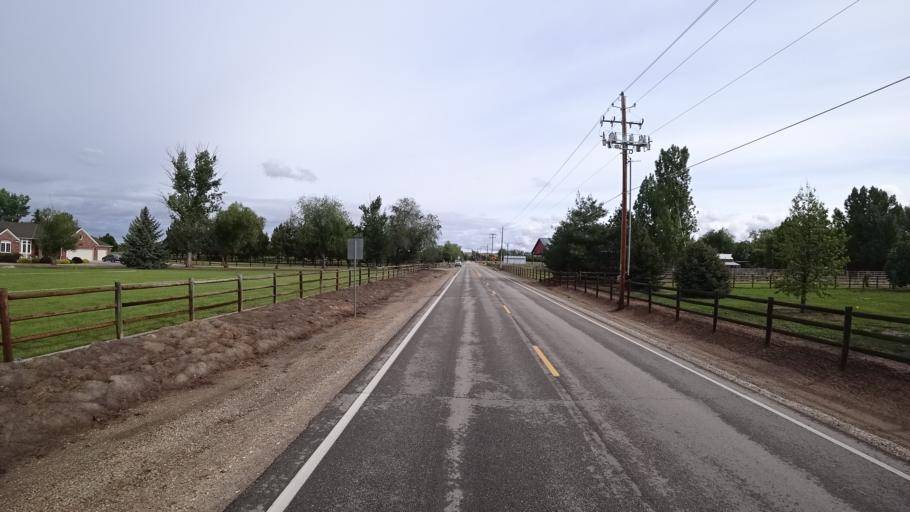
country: US
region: Idaho
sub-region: Ada County
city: Eagle
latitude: 43.7192
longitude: -116.3792
